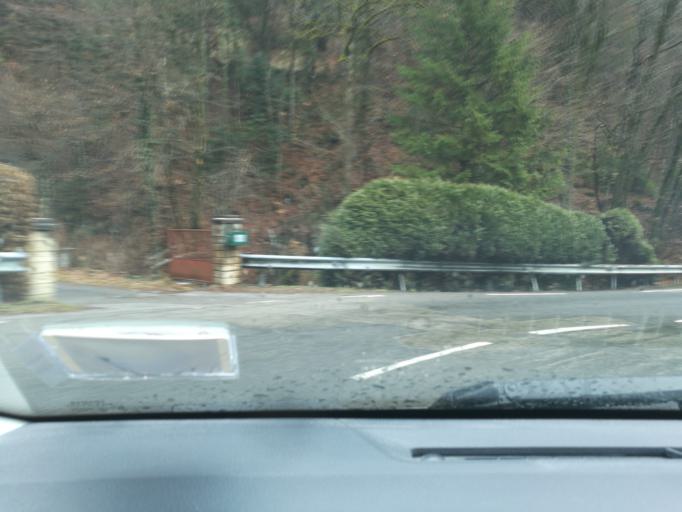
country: FR
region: Rhone-Alpes
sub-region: Departement de la Haute-Savoie
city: Araches-la-Frasse
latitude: 46.0427
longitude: 6.6116
